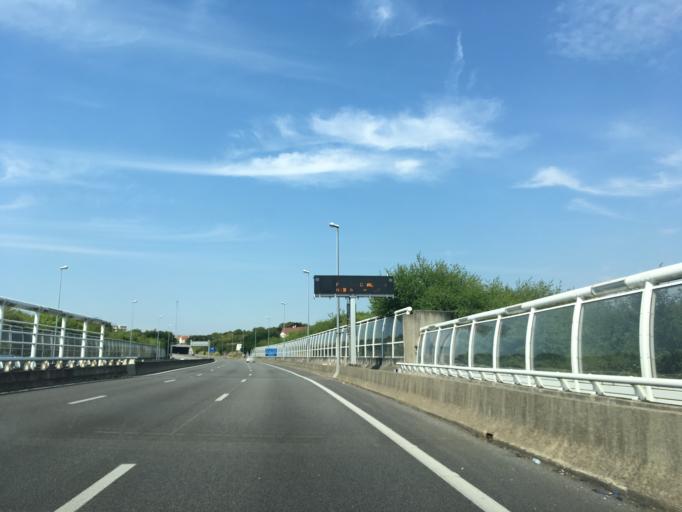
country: FR
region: Ile-de-France
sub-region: Departement des Yvelines
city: Carrieres-sur-Seine
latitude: 48.9090
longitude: 2.1900
